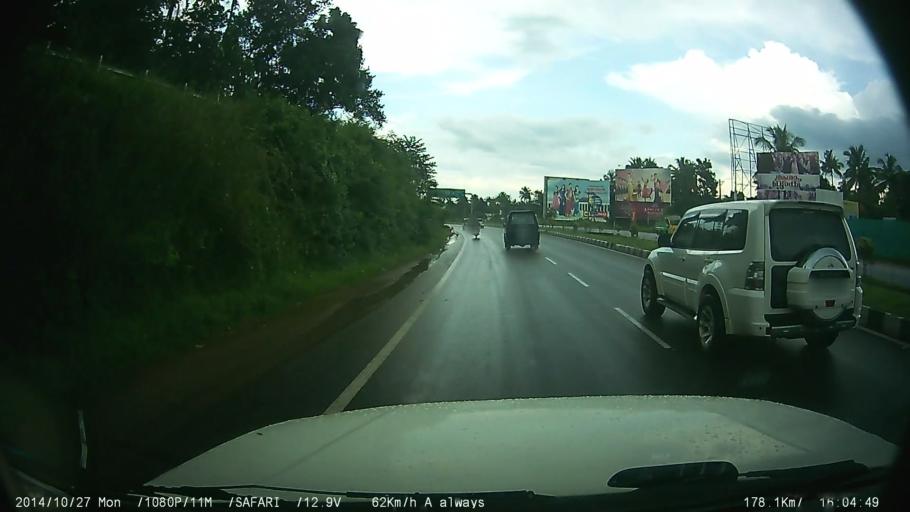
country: IN
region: Kerala
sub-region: Thrissur District
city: Kizhake Chalakudi
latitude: 10.3409
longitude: 76.3221
